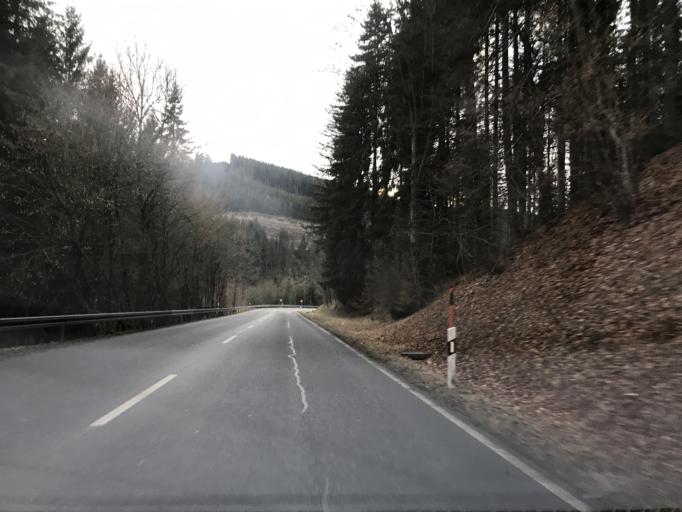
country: DE
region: Baden-Wuerttemberg
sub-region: Freiburg Region
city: Friedenweiler
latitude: 47.9049
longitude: 8.2405
